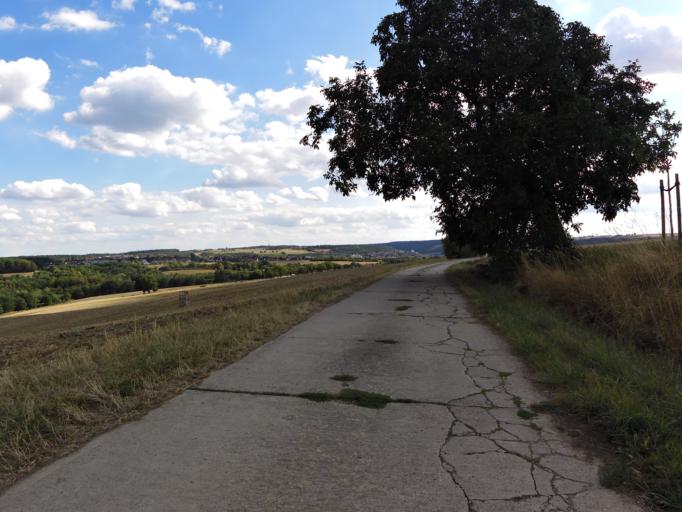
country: DE
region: Bavaria
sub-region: Regierungsbezirk Unterfranken
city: Veitshochheim
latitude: 49.8470
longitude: 9.8838
